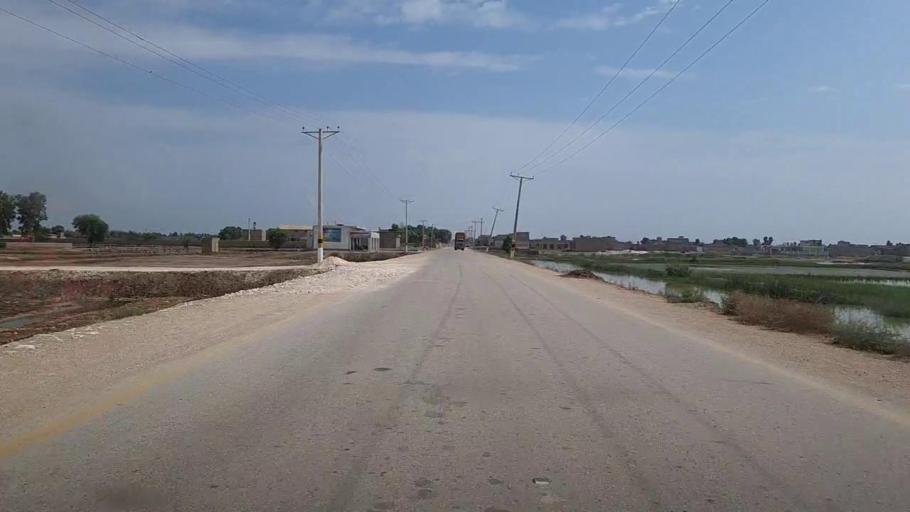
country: PK
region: Sindh
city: Thul
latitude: 28.2495
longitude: 68.7829
